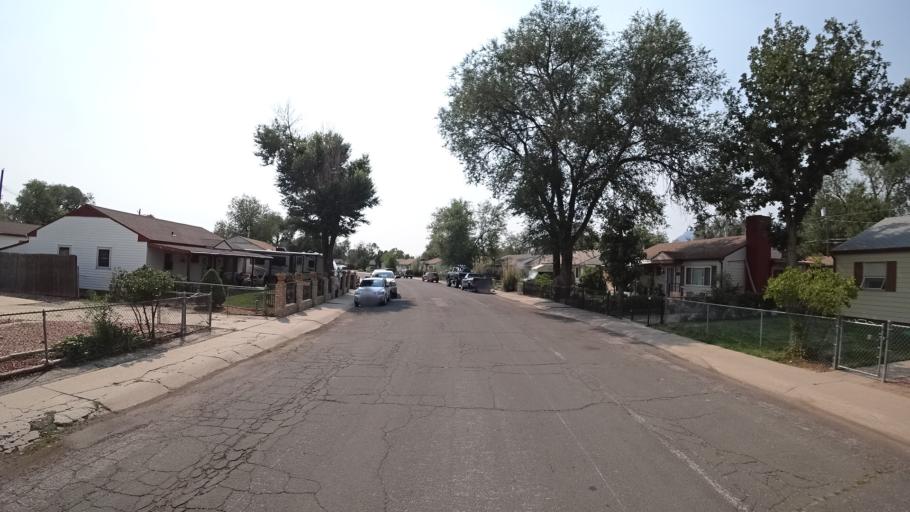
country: US
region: Colorado
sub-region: El Paso County
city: Colorado Springs
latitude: 38.8046
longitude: -104.8066
